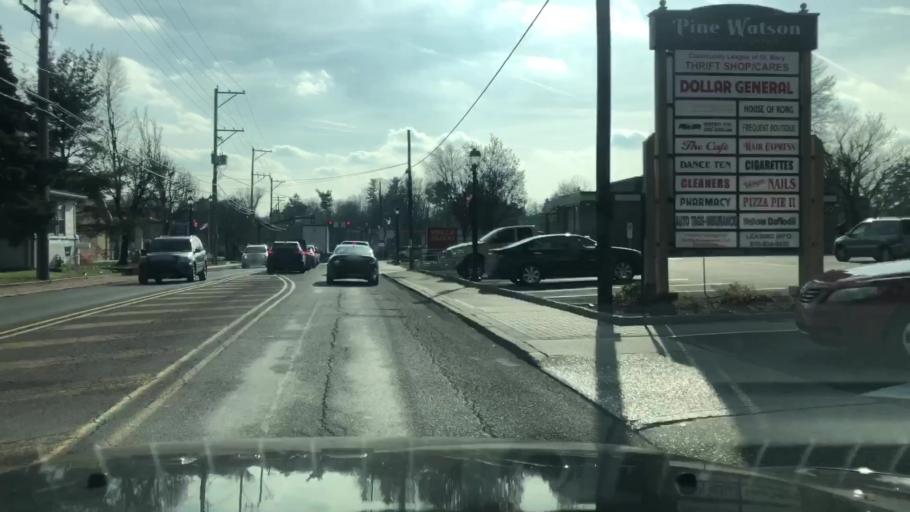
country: US
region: Pennsylvania
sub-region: Bucks County
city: Langhorne
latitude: 40.1779
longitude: -74.9178
